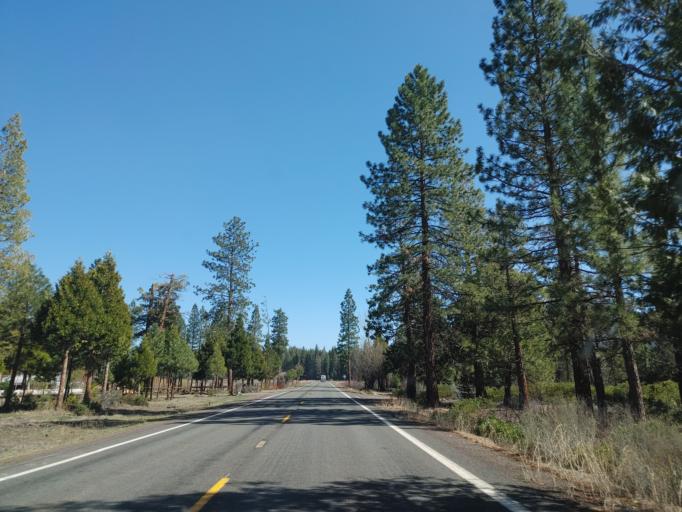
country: US
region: California
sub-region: Shasta County
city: Burney
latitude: 40.7481
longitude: -121.4838
